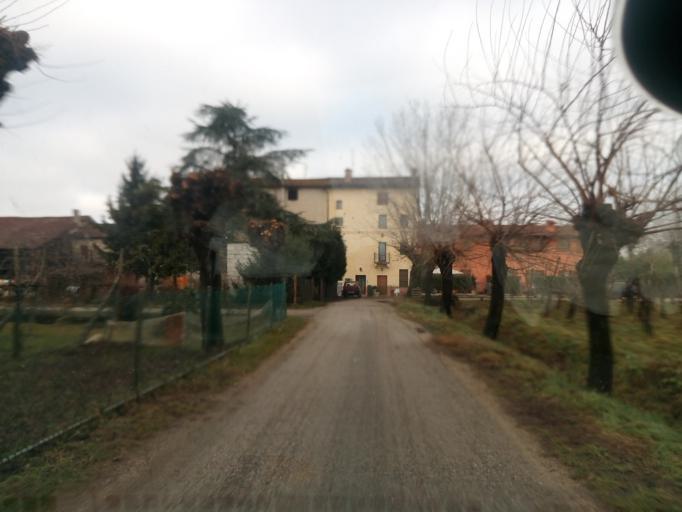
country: IT
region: Veneto
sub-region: Provincia di Vicenza
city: Sandrigo
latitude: 45.6738
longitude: 11.5840
